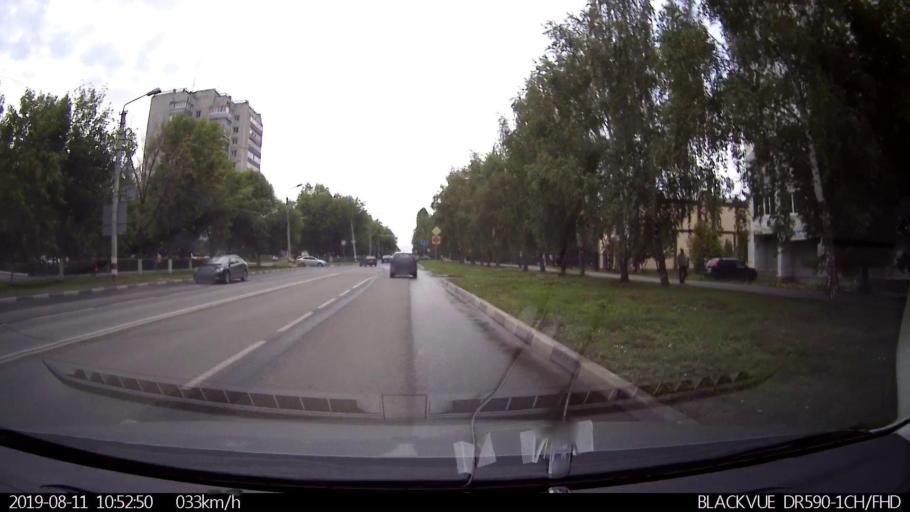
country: RU
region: Ulyanovsk
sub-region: Ulyanovskiy Rayon
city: Ulyanovsk
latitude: 54.2629
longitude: 48.3344
